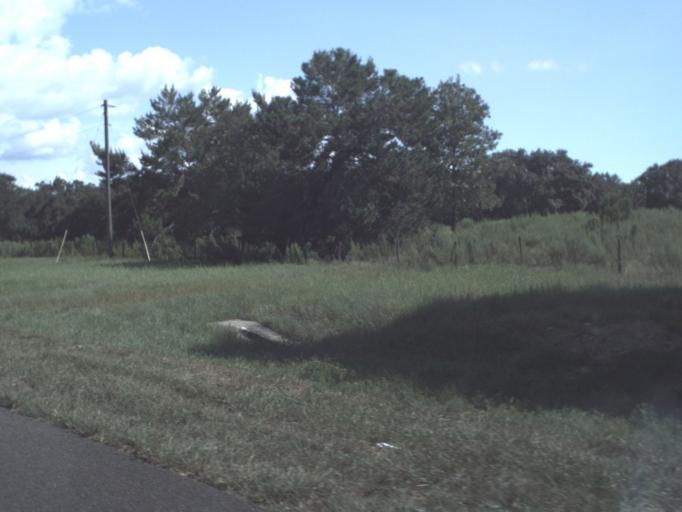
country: US
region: Florida
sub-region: Citrus County
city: Sugarmill Woods
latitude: 28.6792
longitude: -82.4879
